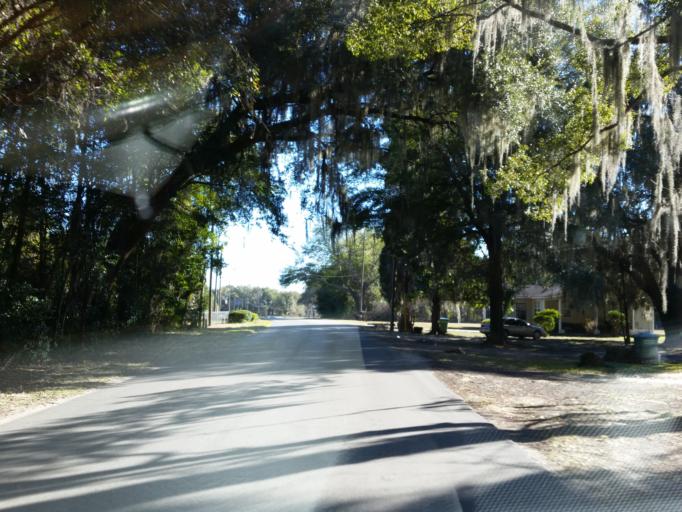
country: US
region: Florida
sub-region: Hamilton County
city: Jasper
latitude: 30.5114
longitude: -82.9531
